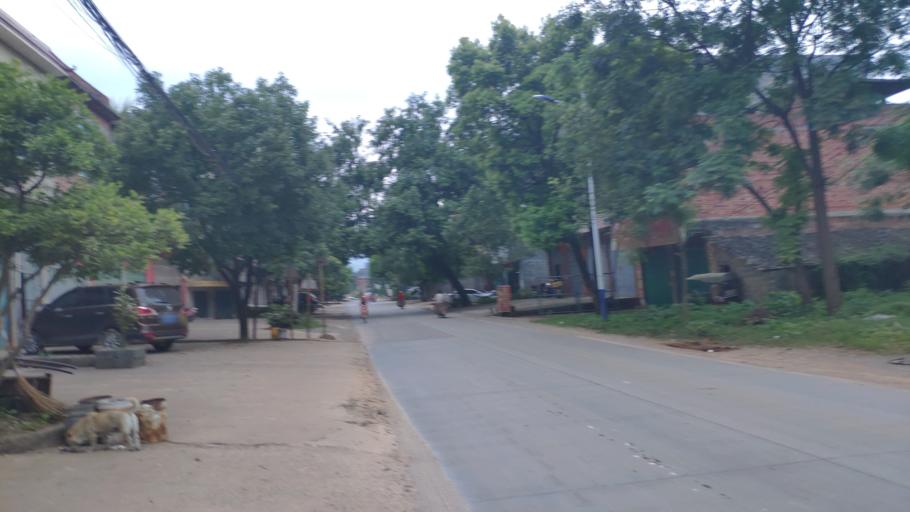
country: CN
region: Hunan
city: Tuojiang
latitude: 25.1867
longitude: 111.5940
